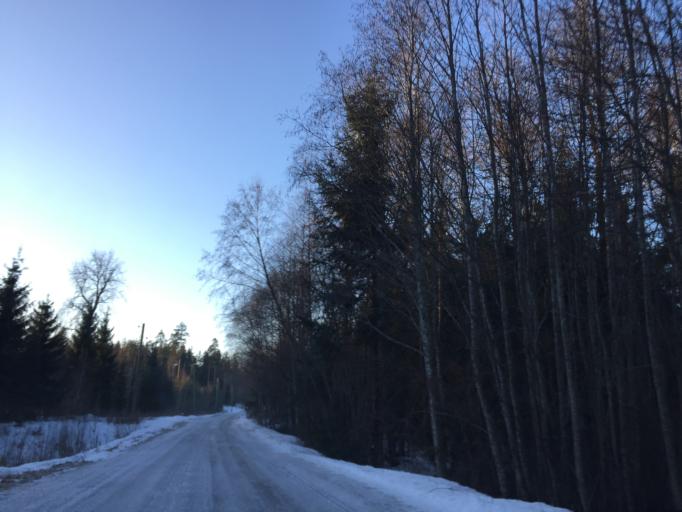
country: LV
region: Kegums
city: Kegums
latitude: 56.7393
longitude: 24.6656
